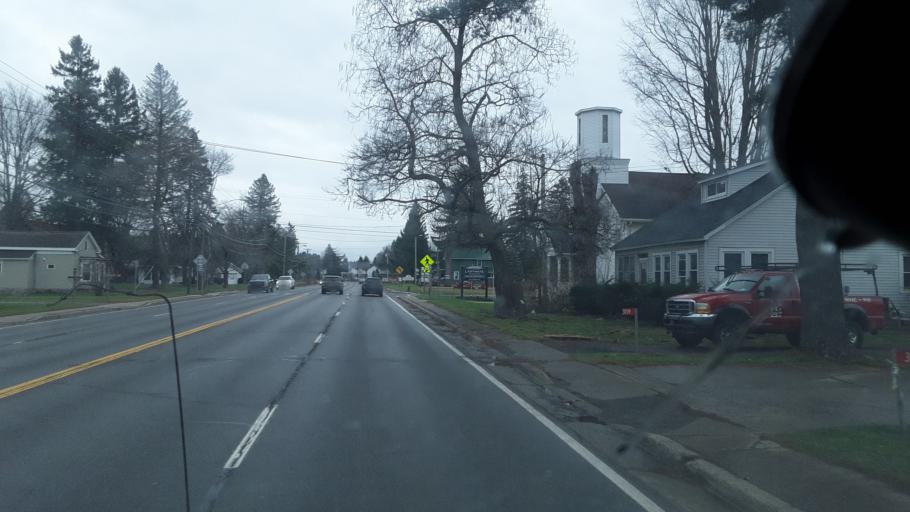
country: US
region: New York
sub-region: Cattaraugus County
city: Yorkshire
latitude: 42.5301
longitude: -78.4714
